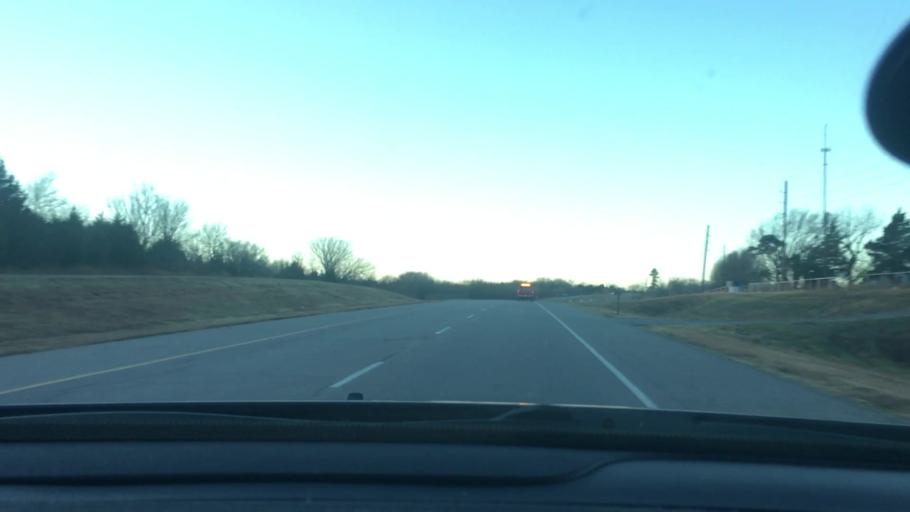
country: US
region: Oklahoma
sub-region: Pontotoc County
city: Ada
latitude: 34.7276
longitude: -96.7109
